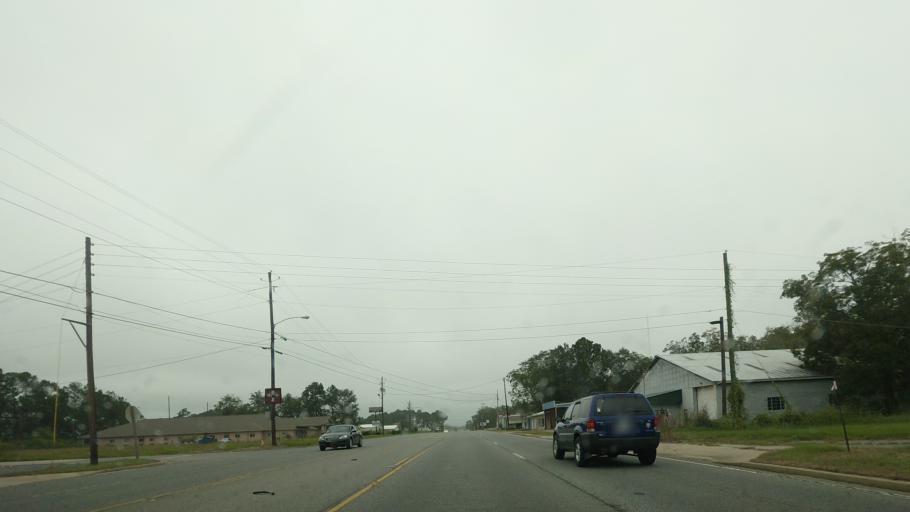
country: US
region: Georgia
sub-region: Irwin County
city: Ocilla
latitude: 31.6177
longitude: -83.2499
